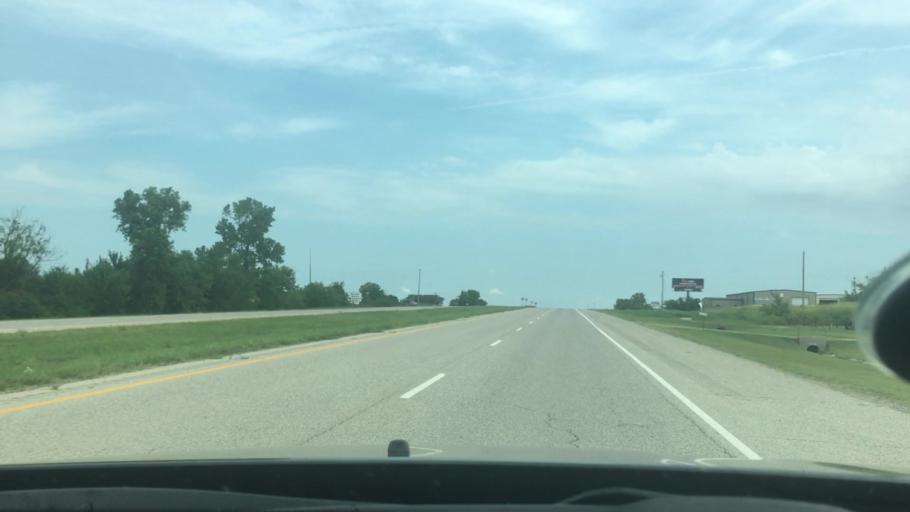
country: US
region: Oklahoma
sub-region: Seminole County
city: Seminole
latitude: 35.1927
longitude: -96.6750
